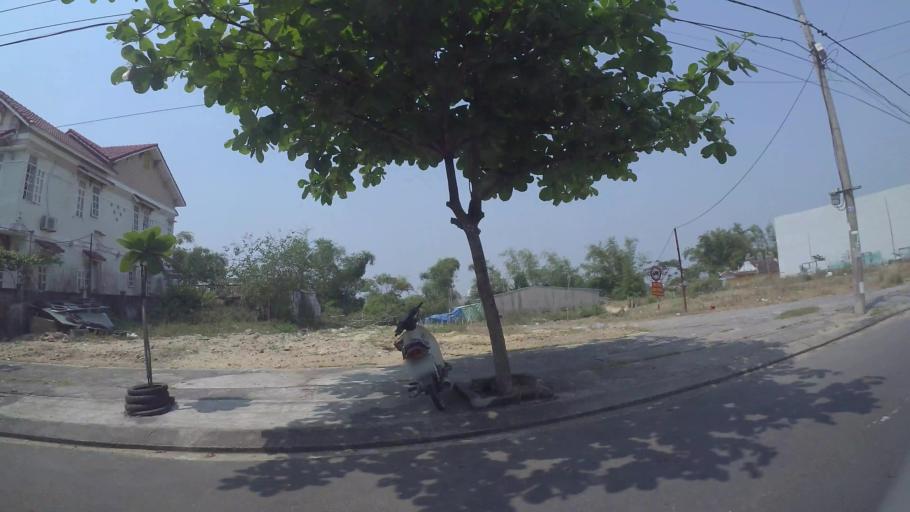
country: VN
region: Da Nang
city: Ngu Hanh Son
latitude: 16.0110
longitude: 108.2522
